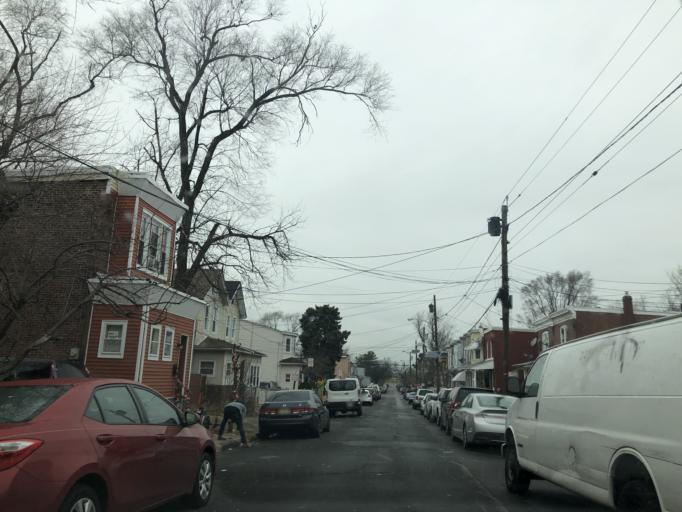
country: US
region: New Jersey
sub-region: Camden County
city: Camden
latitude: 39.9514
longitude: -75.0992
